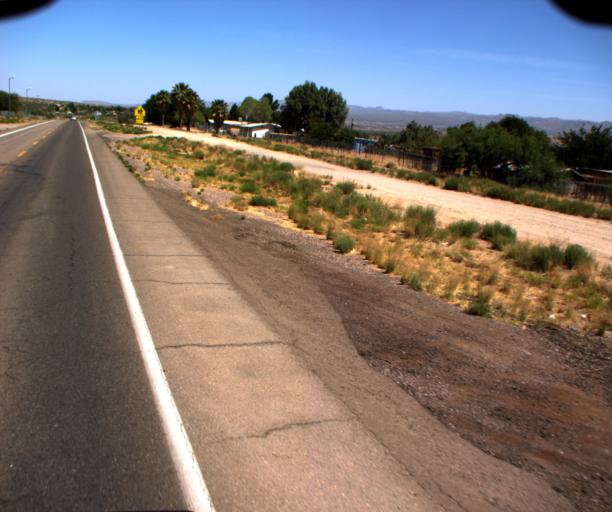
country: US
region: Arizona
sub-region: Graham County
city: Bylas
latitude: 33.1329
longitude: -110.1208
